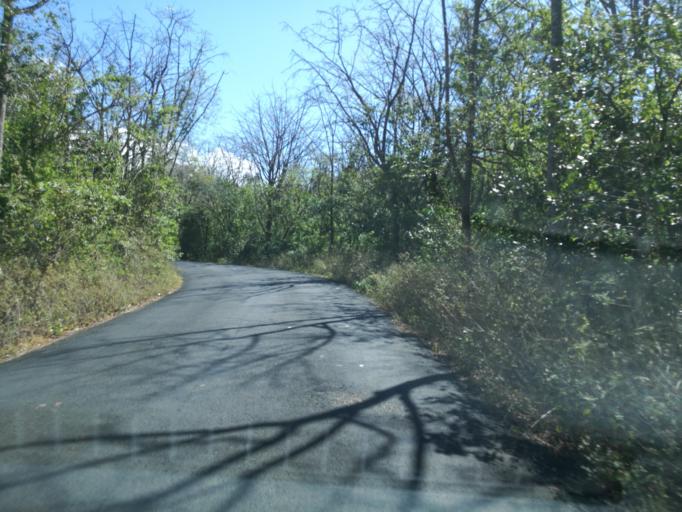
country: CR
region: Guanacaste
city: Liberia
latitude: 10.7491
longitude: -85.3745
